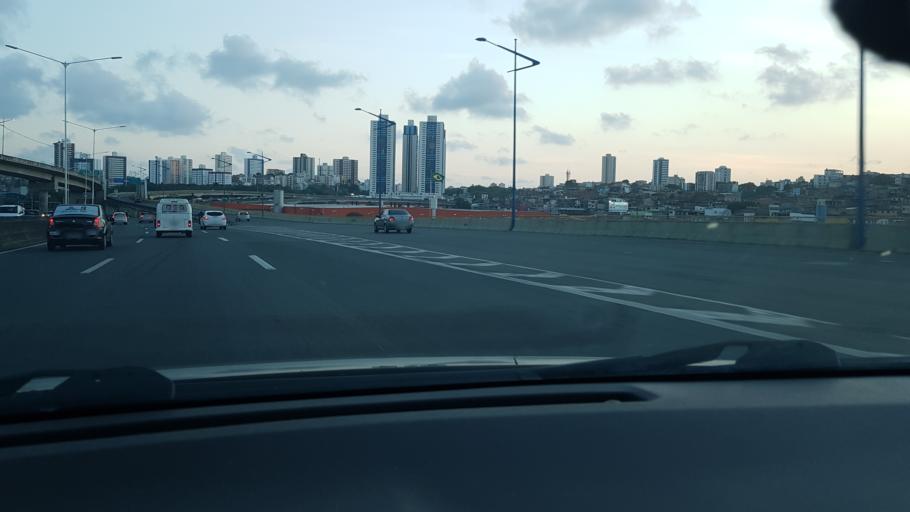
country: BR
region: Bahia
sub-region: Salvador
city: Salvador
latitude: -12.9638
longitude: -38.4768
